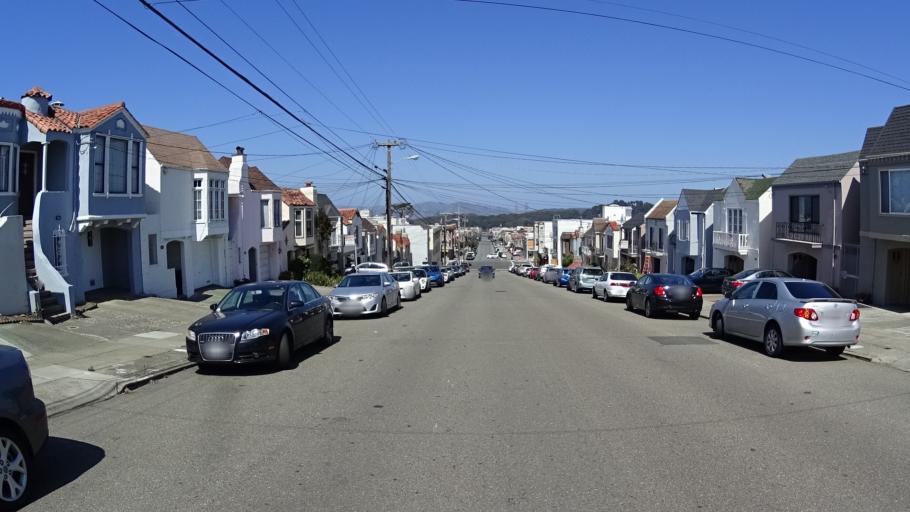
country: US
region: California
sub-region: San Mateo County
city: Daly City
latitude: 37.7529
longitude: -122.4796
